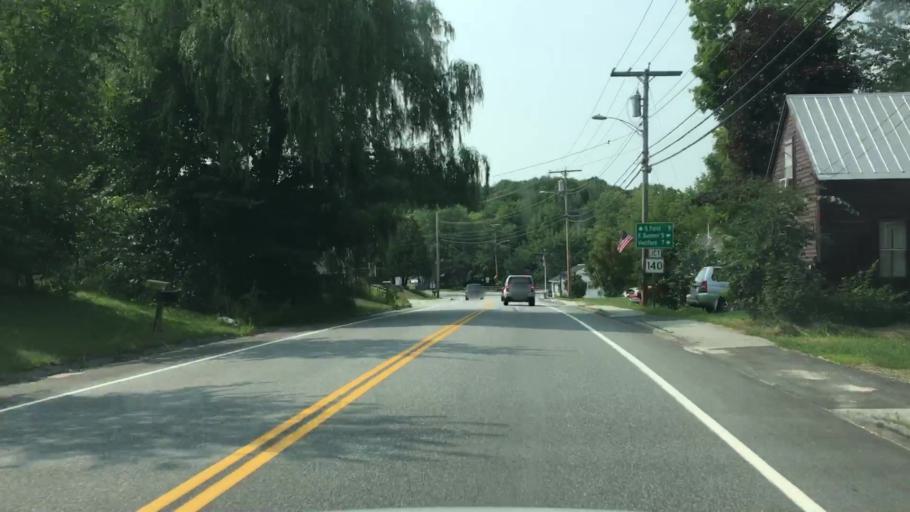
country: US
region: Maine
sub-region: Oxford County
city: Buckfield
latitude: 44.2889
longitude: -70.3635
